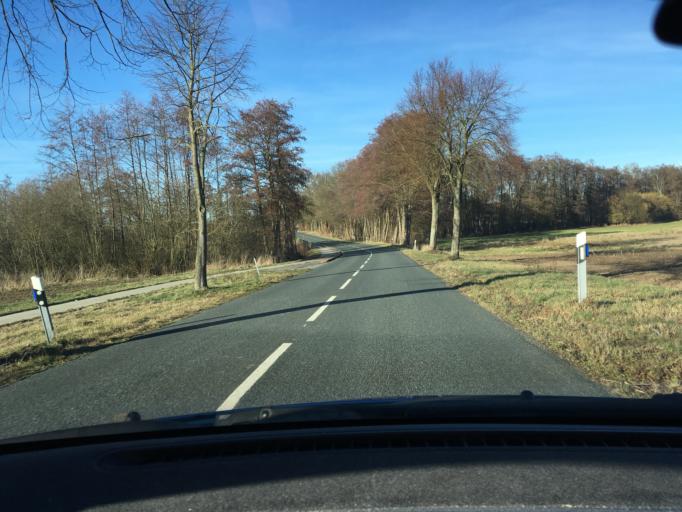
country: DE
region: Lower Saxony
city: Melbeck
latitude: 53.1683
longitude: 10.3821
